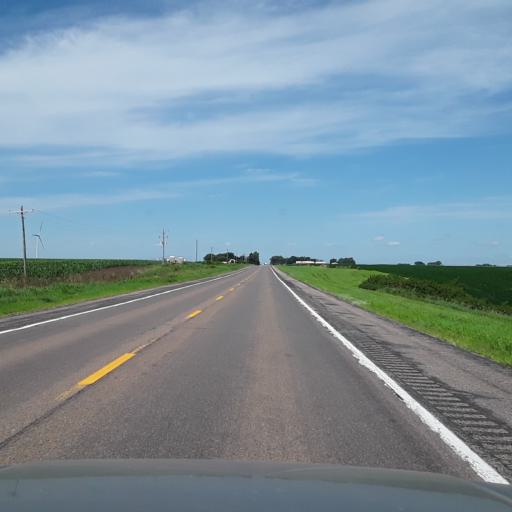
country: US
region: Nebraska
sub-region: Seward County
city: Seward
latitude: 40.9017
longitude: -97.1608
